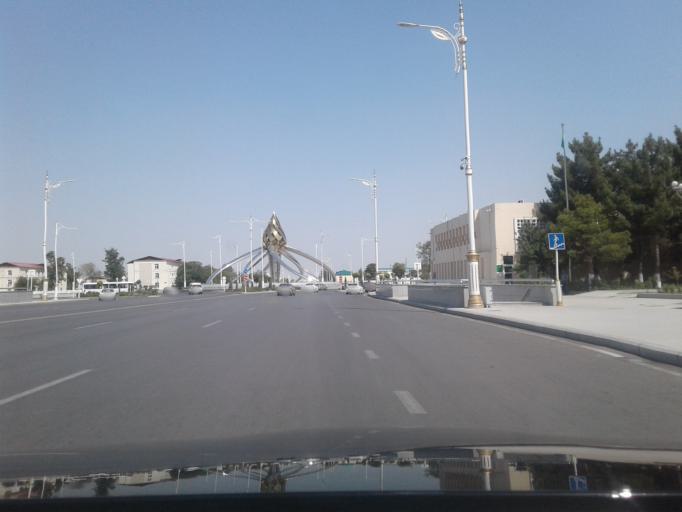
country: TM
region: Ahal
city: Ashgabat
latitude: 37.9223
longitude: 58.3875
